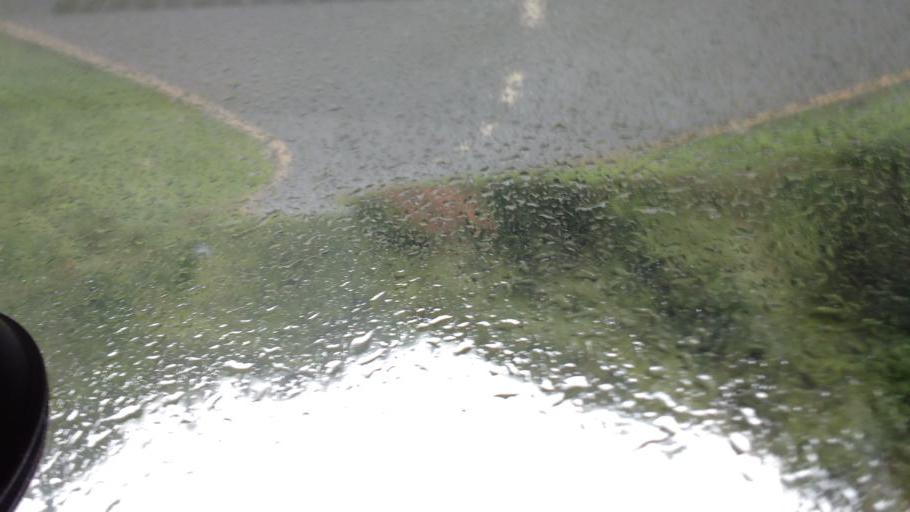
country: IN
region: Meghalaya
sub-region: East Khasi Hills
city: Shillong
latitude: 25.4518
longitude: 91.8190
